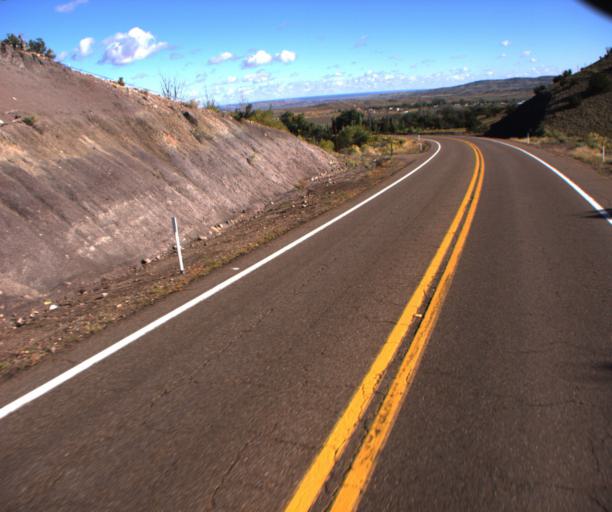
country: US
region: Arizona
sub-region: Apache County
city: Saint Johns
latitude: 34.4610
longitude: -109.6197
